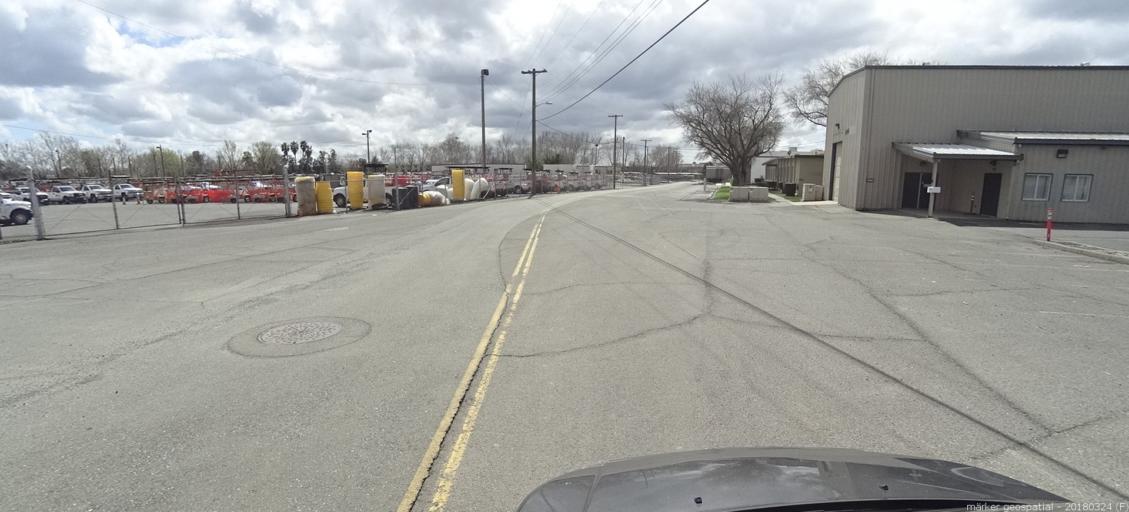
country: US
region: California
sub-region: Sacramento County
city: North Highlands
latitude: 38.6723
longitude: -121.3921
